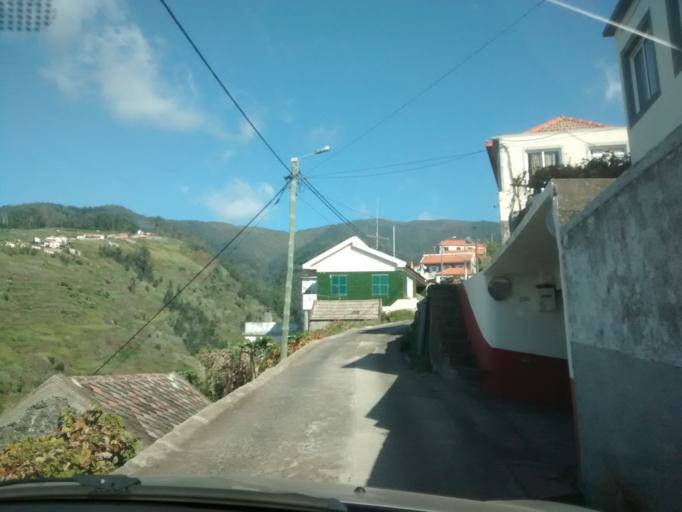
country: PT
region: Madeira
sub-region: Calheta
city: Arco da Calheta
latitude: 32.7283
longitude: -17.1643
